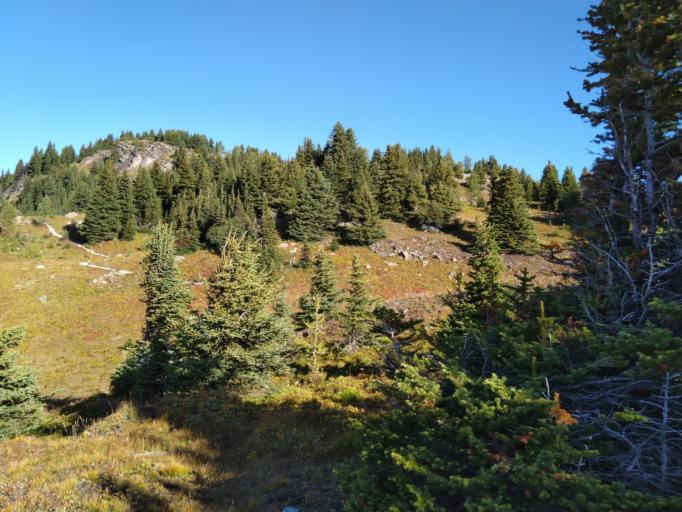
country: CA
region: Alberta
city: Banff
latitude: 51.0641
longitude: -115.7815
